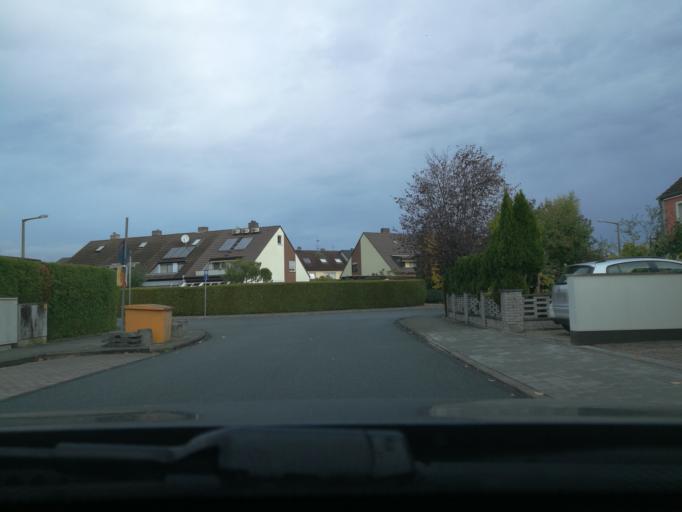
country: DE
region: Bavaria
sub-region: Regierungsbezirk Mittelfranken
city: Zirndorf
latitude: 49.4792
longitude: 10.9493
